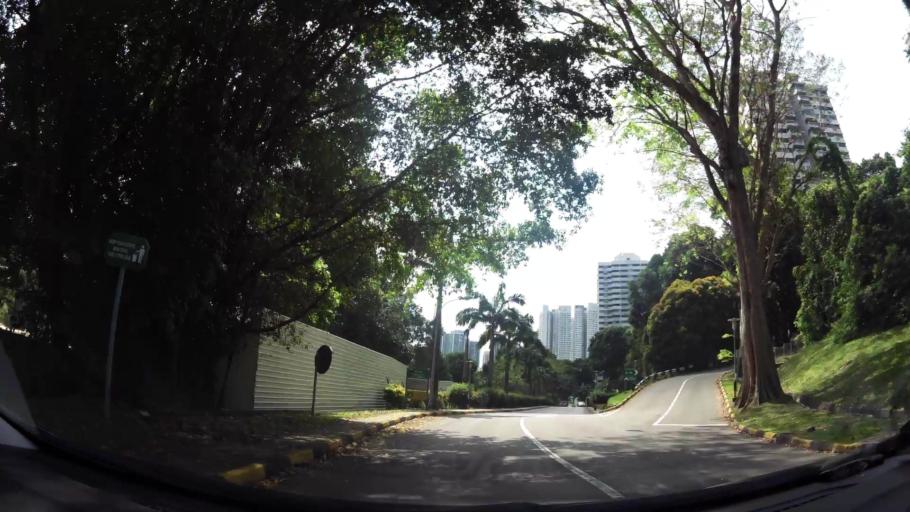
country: SG
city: Singapore
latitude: 1.3437
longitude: 103.8419
